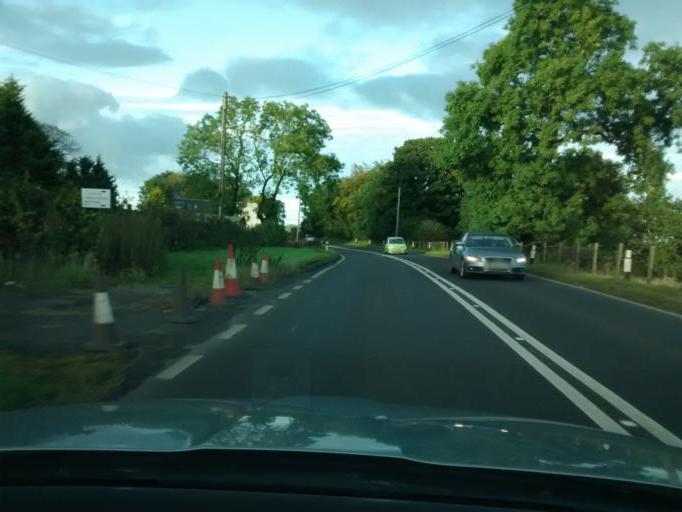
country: GB
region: Scotland
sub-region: Renfrewshire
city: Lochwinnoch
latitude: 55.7968
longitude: -4.5956
